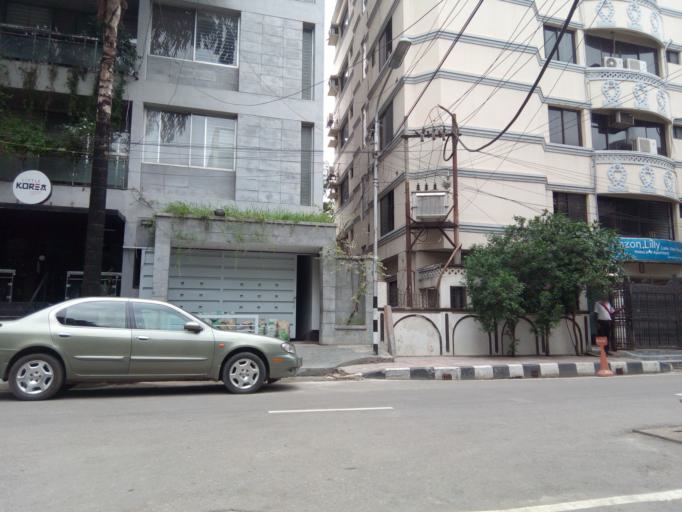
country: BD
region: Dhaka
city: Paltan
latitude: 23.7926
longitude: 90.4093
